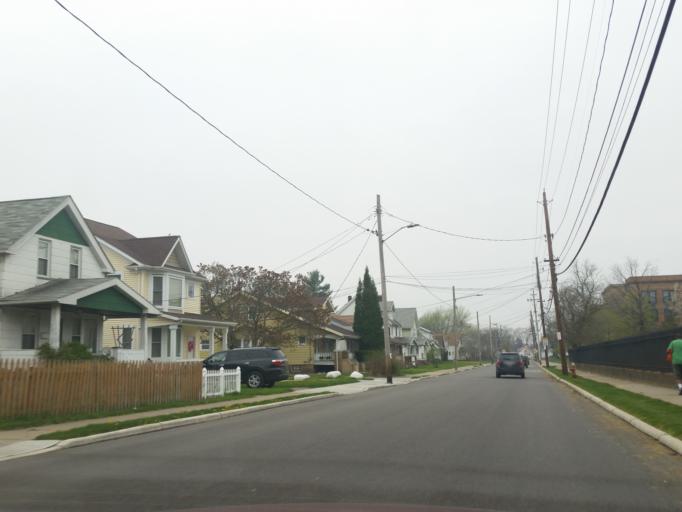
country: US
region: Ohio
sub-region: Cuyahoga County
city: Brooklyn
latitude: 41.4300
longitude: -81.7187
